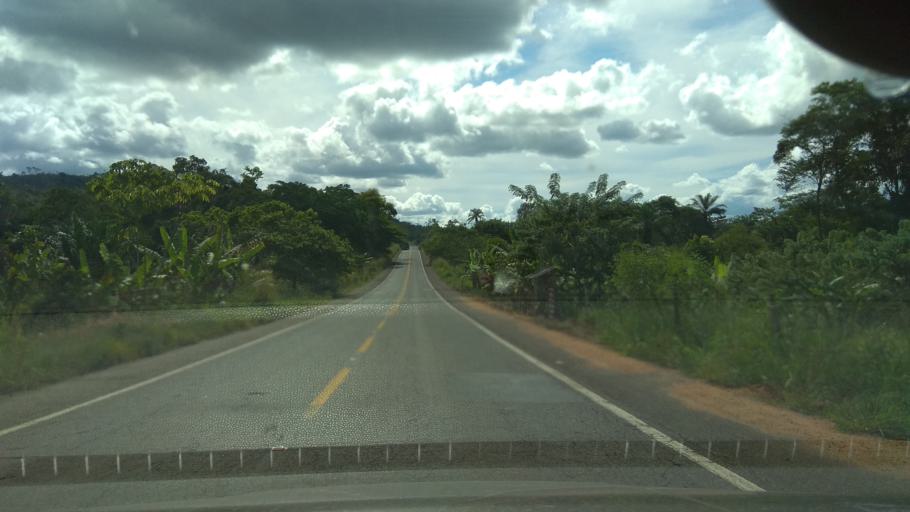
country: BR
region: Bahia
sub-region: Ubaitaba
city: Ubaitaba
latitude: -14.2531
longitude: -39.3556
